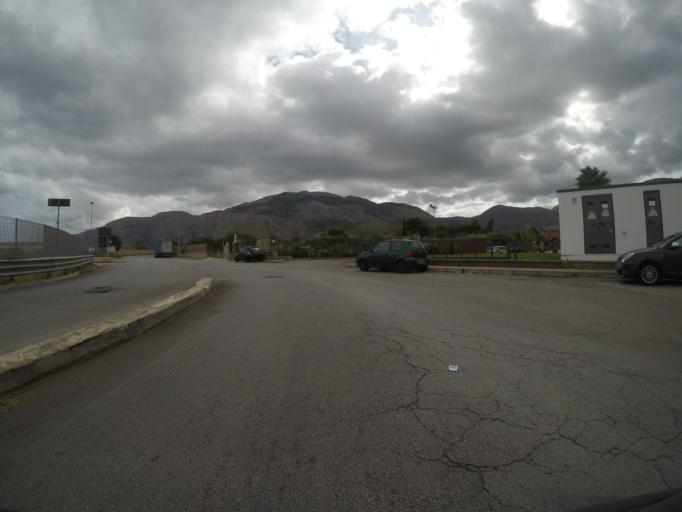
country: IT
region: Sicily
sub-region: Palermo
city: Capaci
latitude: 38.1726
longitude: 13.2163
